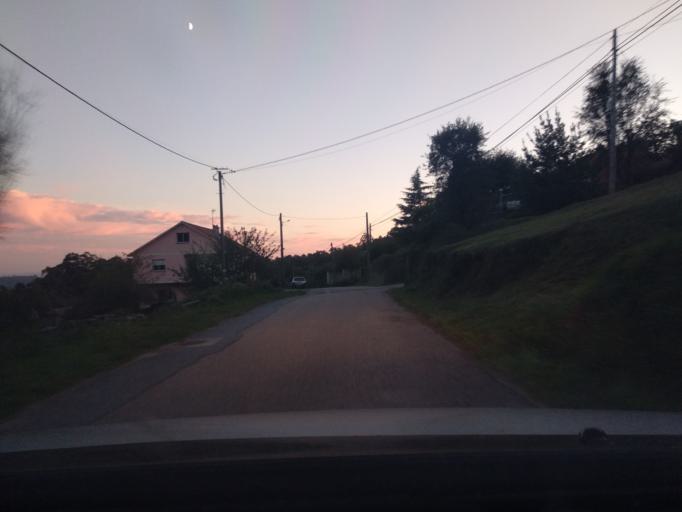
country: ES
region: Galicia
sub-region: Provincia de Pontevedra
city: Moana
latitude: 42.3039
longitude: -8.6994
